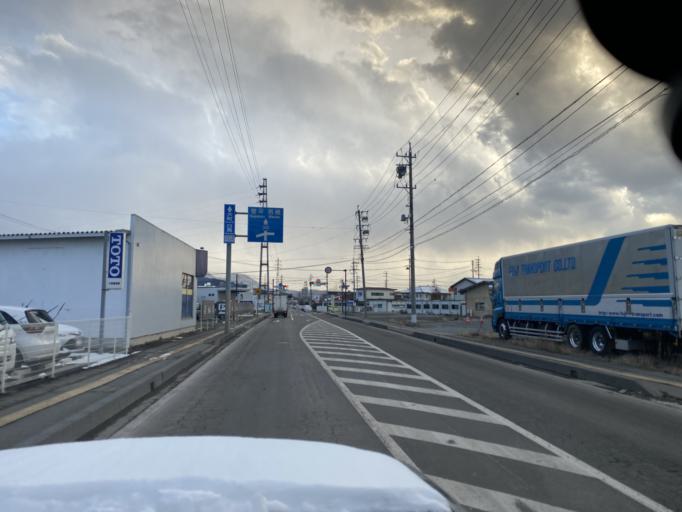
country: JP
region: Nagano
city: Nagano-shi
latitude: 36.6347
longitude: 138.2402
